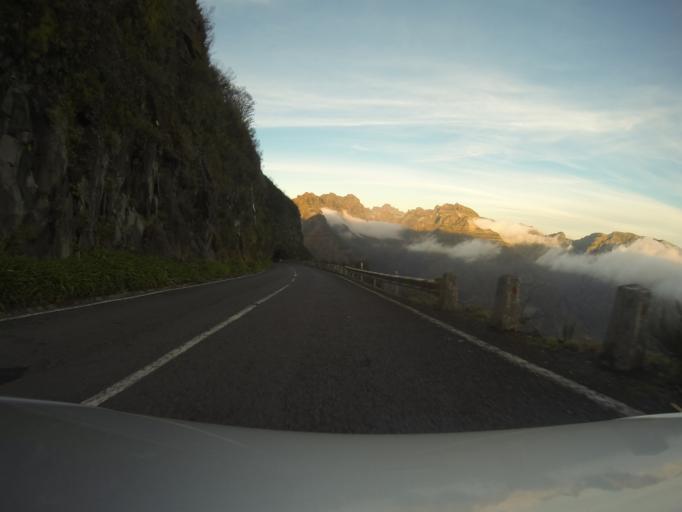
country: PT
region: Madeira
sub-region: Sao Vicente
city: Sao Vicente
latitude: 32.7471
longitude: -17.0387
